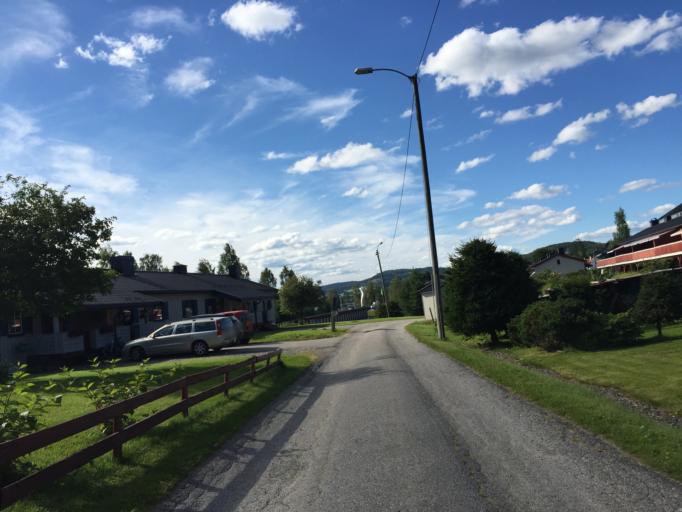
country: NO
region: Hedmark
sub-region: Kongsvinger
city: Kongsvinger
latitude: 60.2003
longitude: 11.9825
